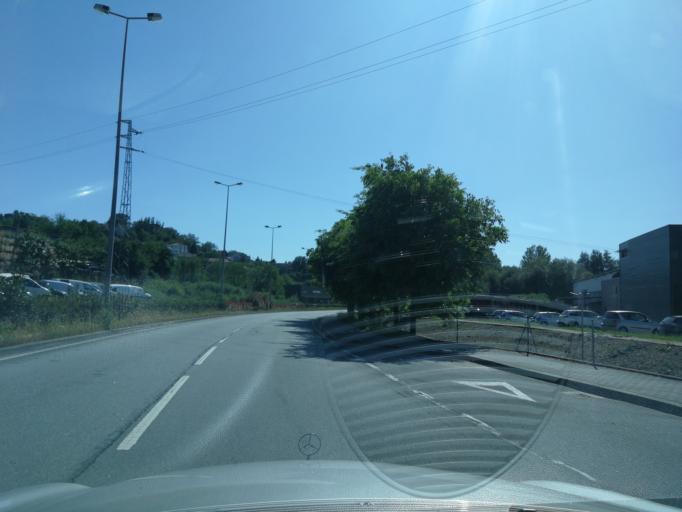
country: PT
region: Braga
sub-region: Braga
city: Adaufe
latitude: 41.5609
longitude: -8.3866
